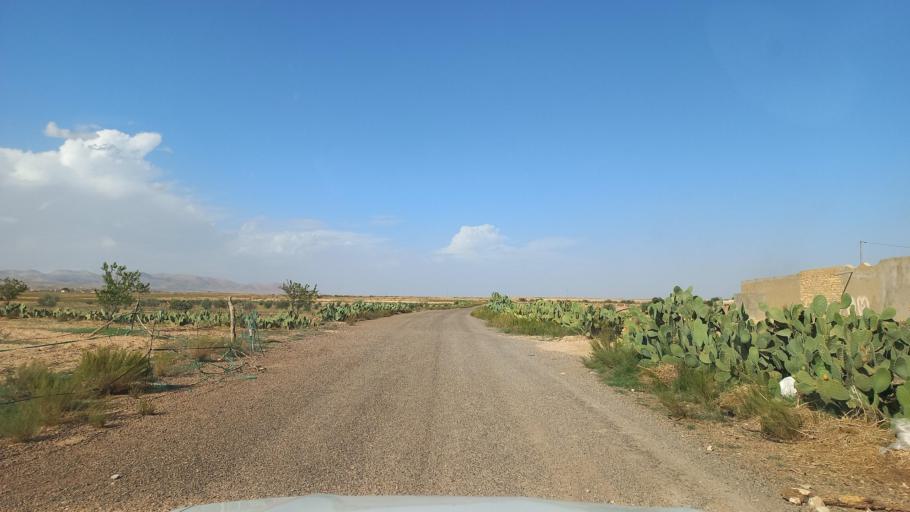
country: TN
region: Al Qasrayn
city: Kasserine
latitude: 35.3179
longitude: 9.0142
